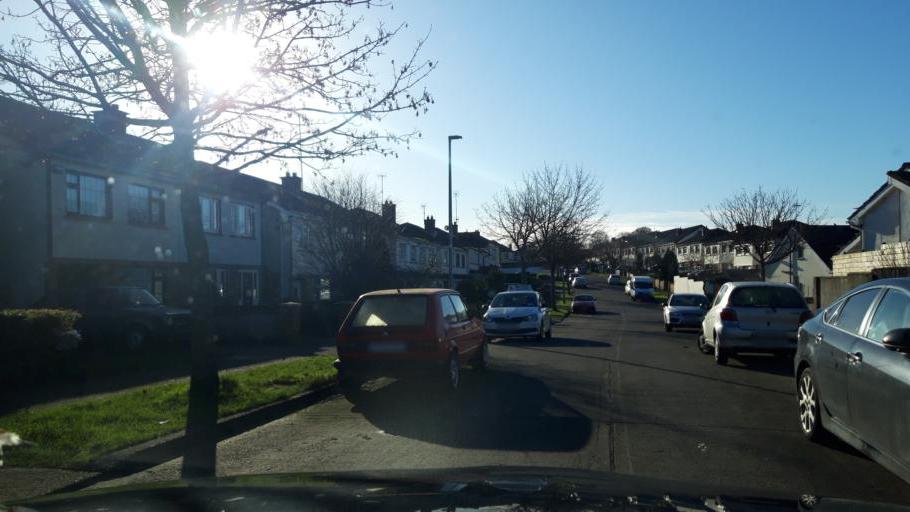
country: IE
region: Leinster
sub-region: Fingal County
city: Swords
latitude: 53.4541
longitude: -6.2486
